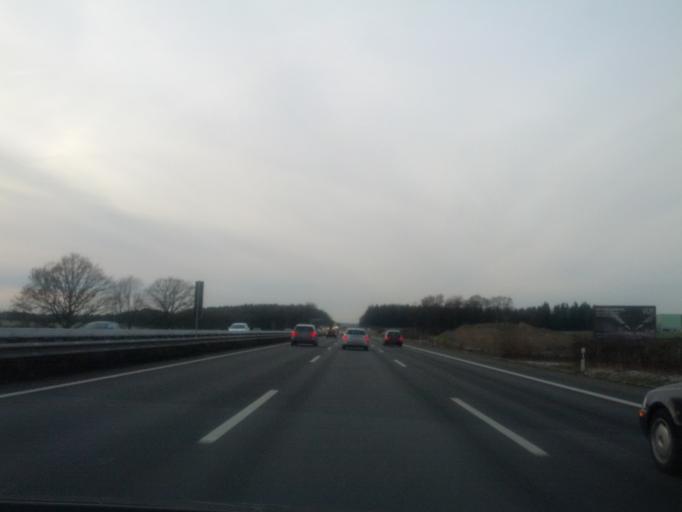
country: DE
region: Lower Saxony
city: Wenzendorf
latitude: 53.3709
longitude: 9.7954
